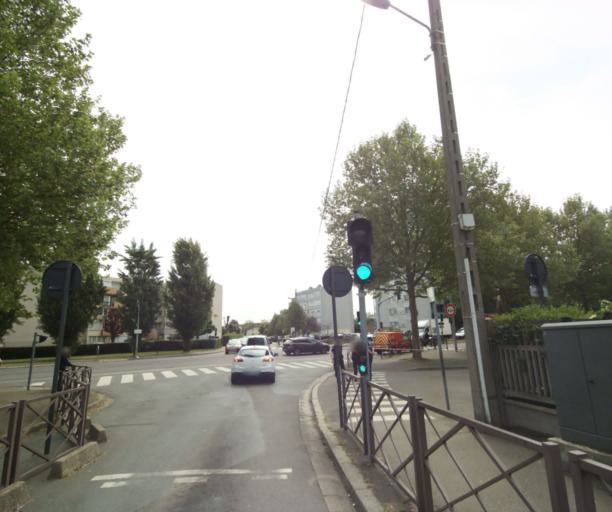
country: FR
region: Ile-de-France
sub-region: Departement des Yvelines
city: Les Mureaux
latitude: 48.9951
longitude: 1.9132
